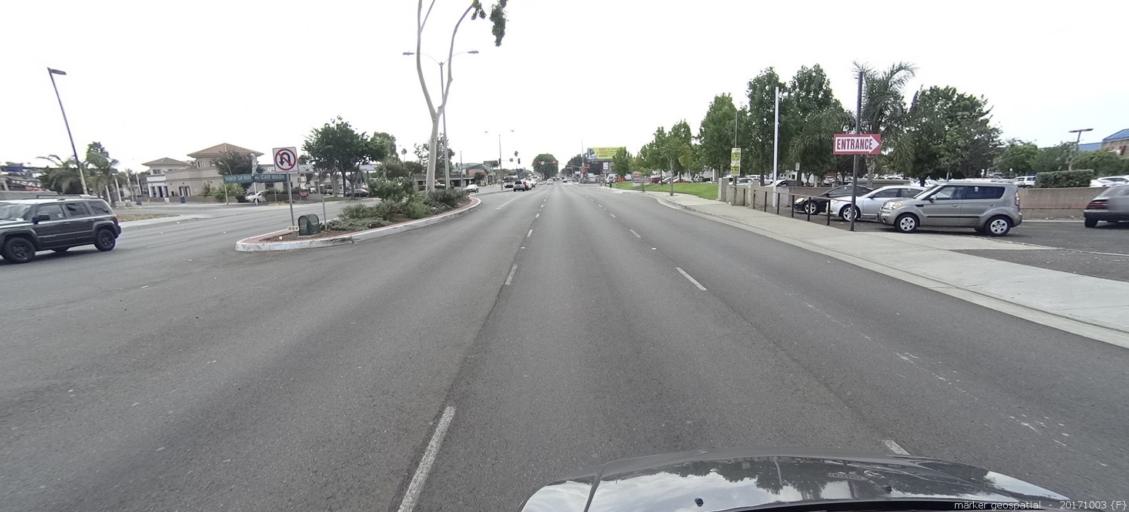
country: US
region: California
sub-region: Orange County
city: Garden Grove
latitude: 33.7613
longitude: -117.9203
